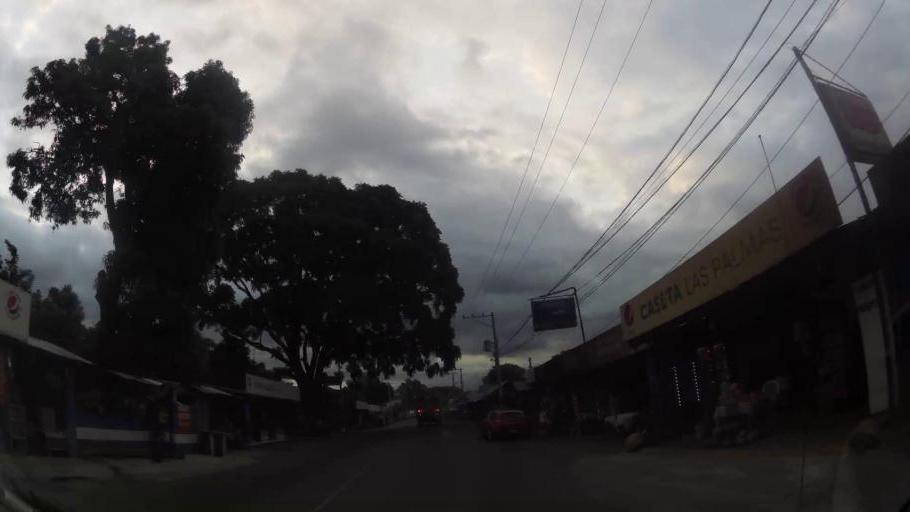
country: GT
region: Suchitepeque
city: Patulul
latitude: 14.3654
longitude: -91.0996
